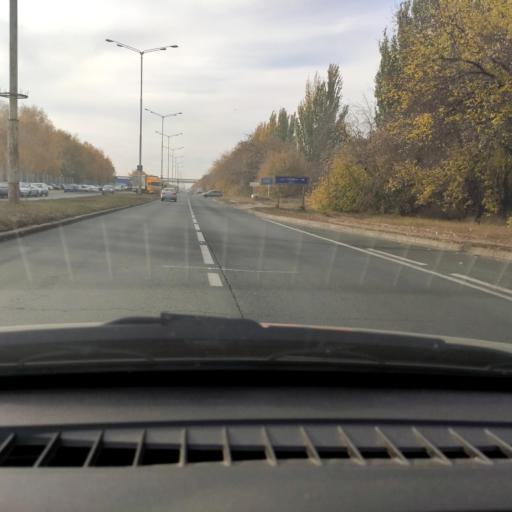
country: RU
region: Samara
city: Tol'yatti
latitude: 53.5699
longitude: 49.2553
